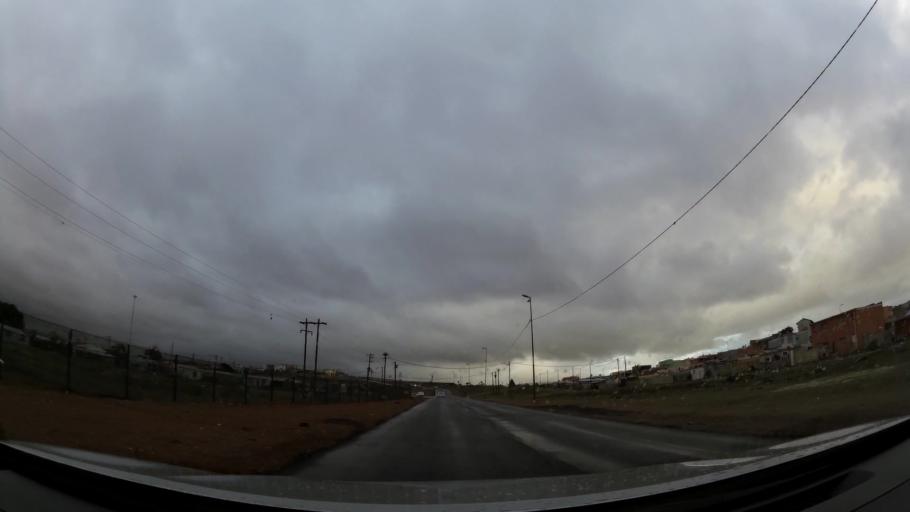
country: ZA
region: Eastern Cape
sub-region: Nelson Mandela Bay Metropolitan Municipality
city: Port Elizabeth
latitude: -33.8881
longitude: 25.5575
